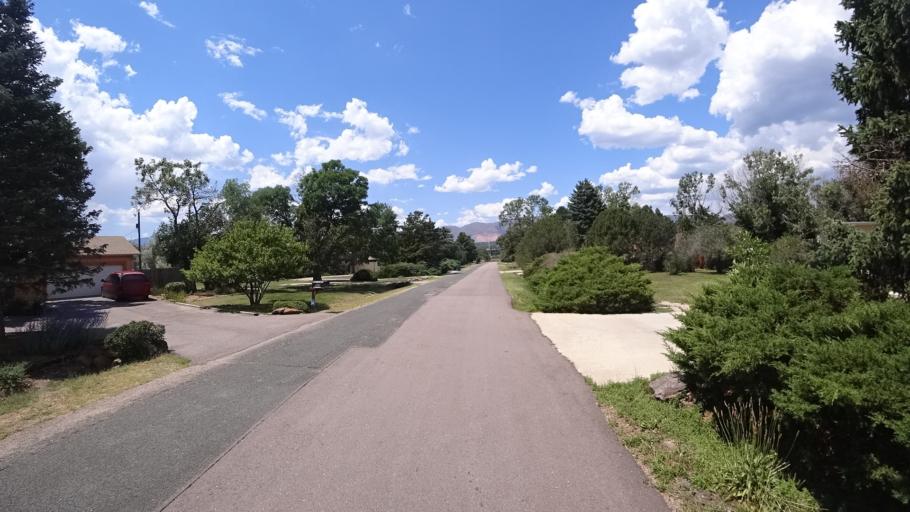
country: US
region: Colorado
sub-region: El Paso County
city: Air Force Academy
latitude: 38.9370
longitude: -104.8075
